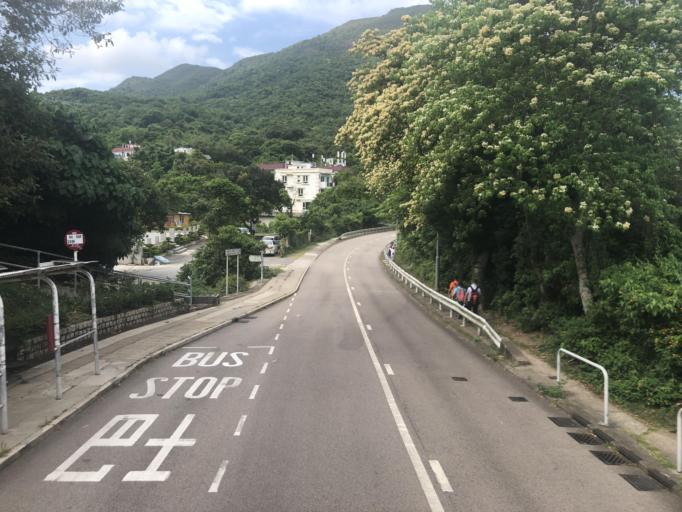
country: HK
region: Sai Kung
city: Sai Kung
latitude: 22.3912
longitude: 114.3079
